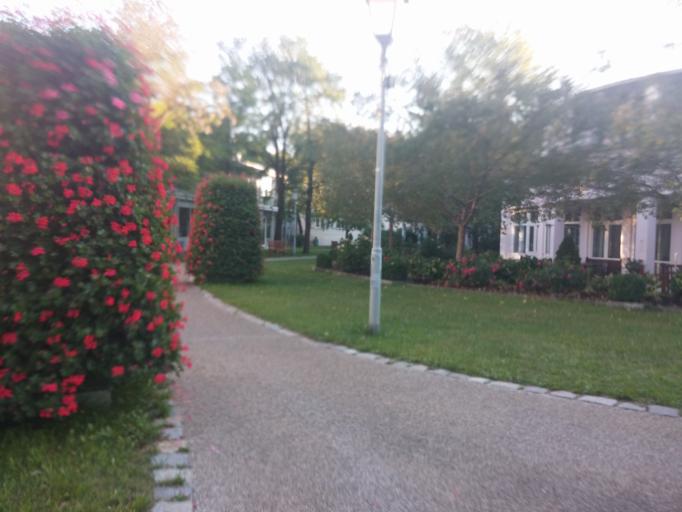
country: DE
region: Bavaria
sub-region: Upper Bavaria
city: Haar
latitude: 48.1104
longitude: 11.7274
